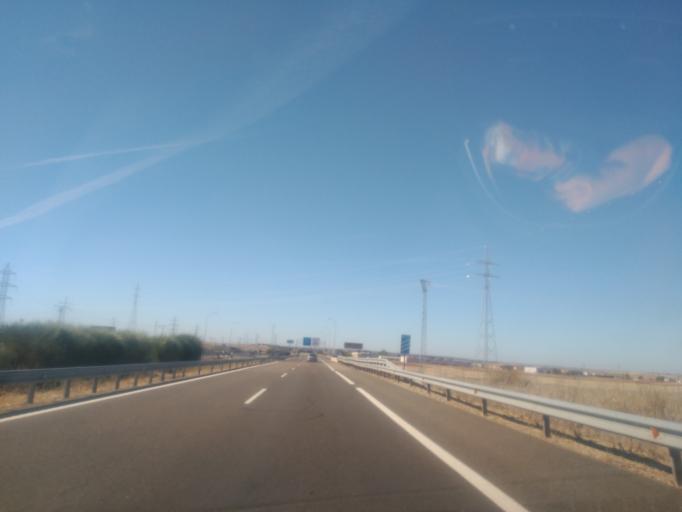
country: ES
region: Castille and Leon
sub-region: Provincia de Salamanca
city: Villares de la Reina
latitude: 41.0005
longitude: -5.6554
